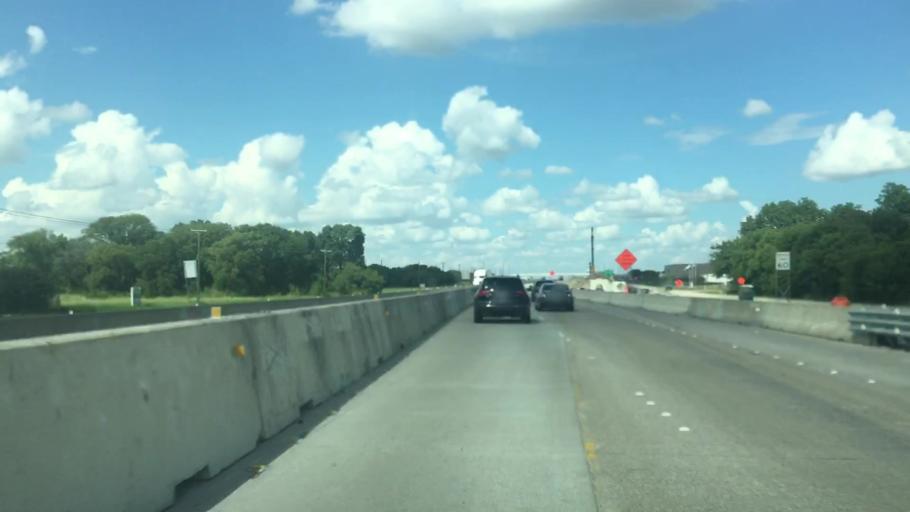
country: US
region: Texas
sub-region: Ellis County
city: Oak Leaf
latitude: 32.4667
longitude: -96.8407
